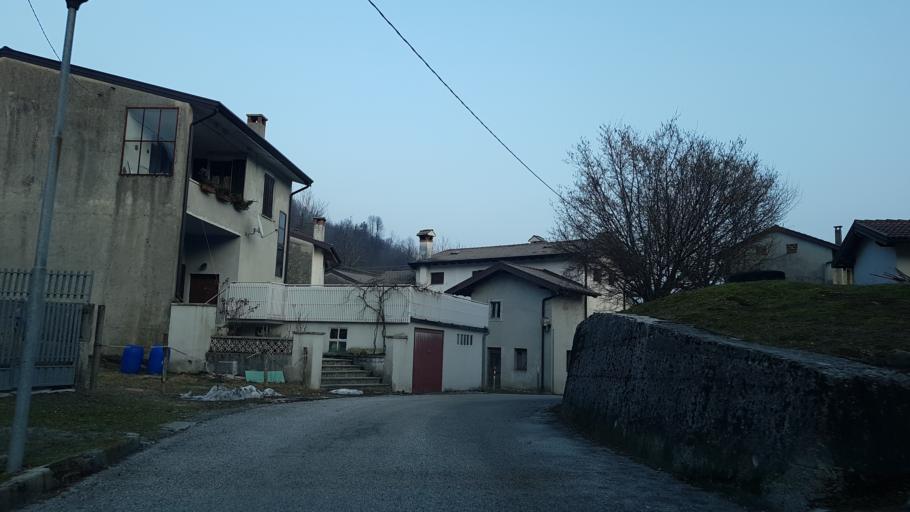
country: IT
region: Friuli Venezia Giulia
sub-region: Provincia di Udine
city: Taipana
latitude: 46.2411
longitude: 13.3857
